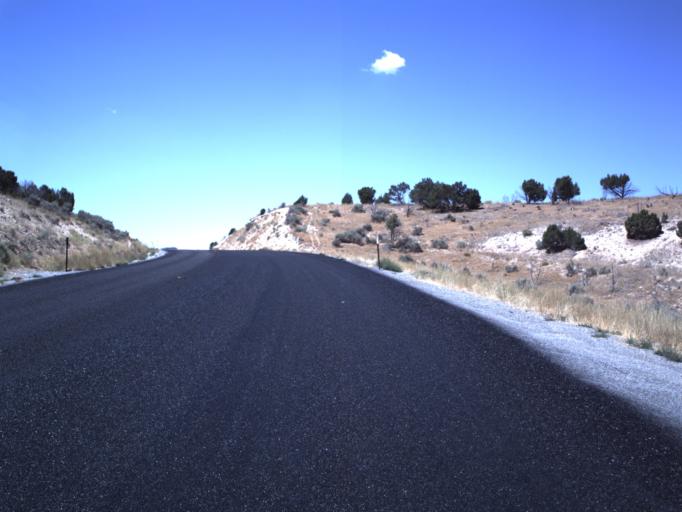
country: US
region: Utah
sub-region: Juab County
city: Nephi
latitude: 39.6982
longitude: -111.9457
